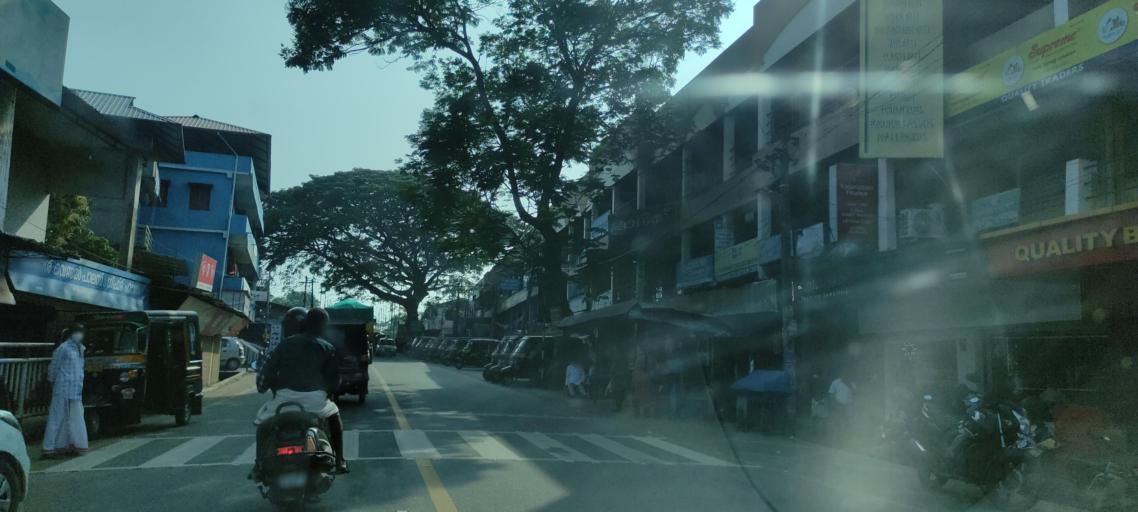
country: IN
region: Kerala
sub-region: Kottayam
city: Changanacheri
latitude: 9.3661
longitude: 76.4773
